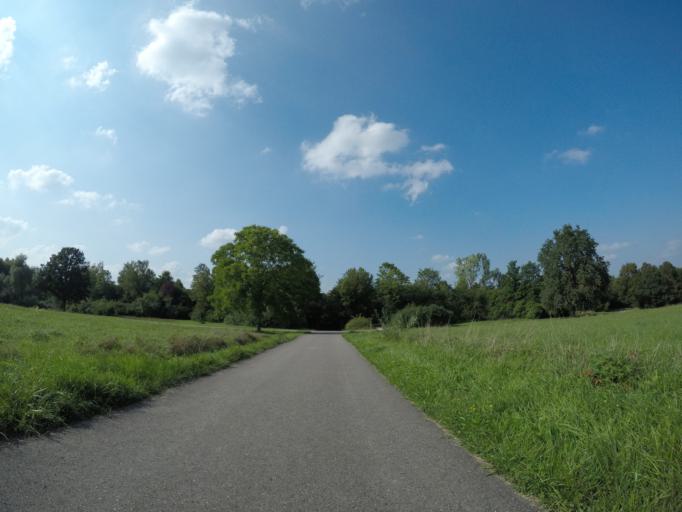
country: DE
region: Baden-Wuerttemberg
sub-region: Tuebingen Region
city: Reutlingen
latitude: 48.4751
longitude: 9.1828
